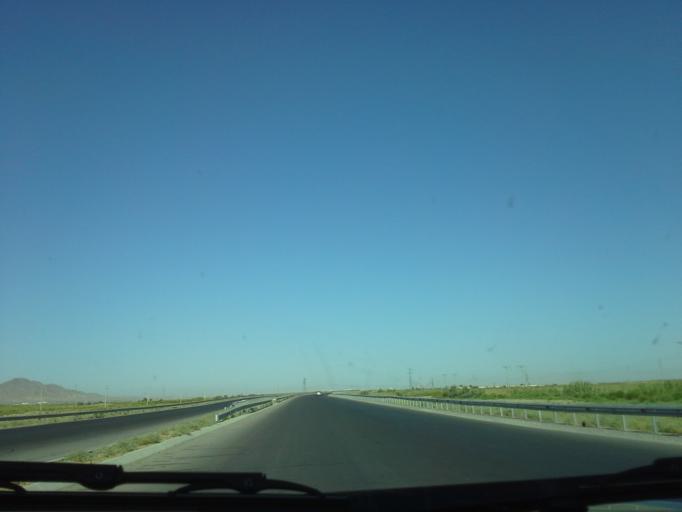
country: TM
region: Balkan
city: Gazanjyk
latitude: 39.2511
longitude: 55.6013
